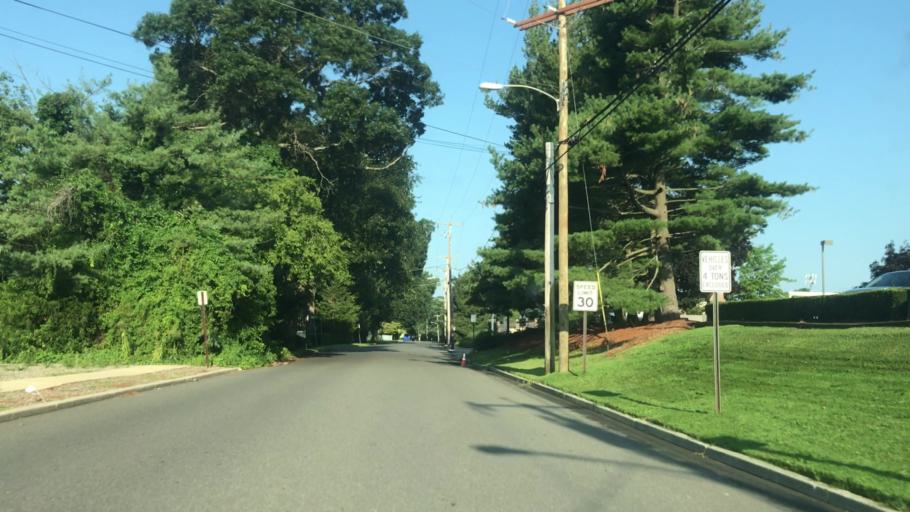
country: US
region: New Jersey
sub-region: Ocean County
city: Pine Beach
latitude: 39.9569
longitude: -74.1708
